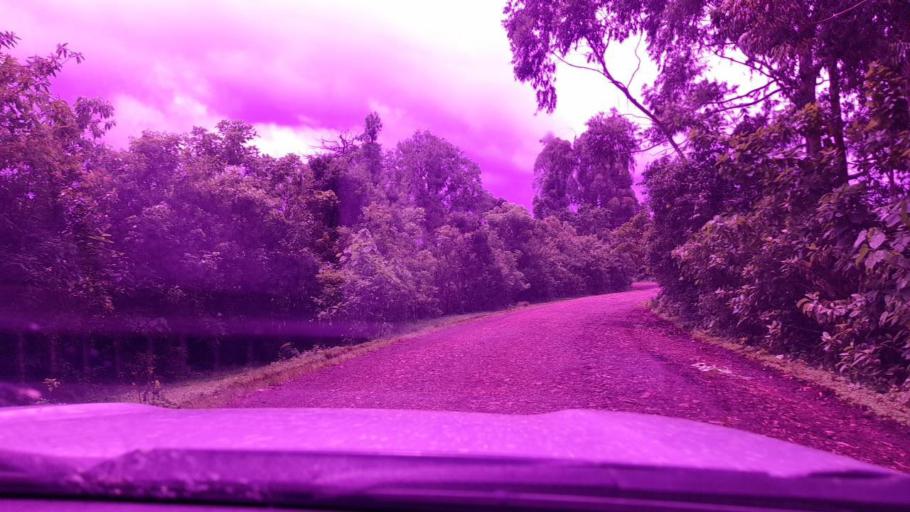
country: ET
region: Southern Nations, Nationalities, and People's Region
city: Tippi
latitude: 7.6178
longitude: 35.5839
